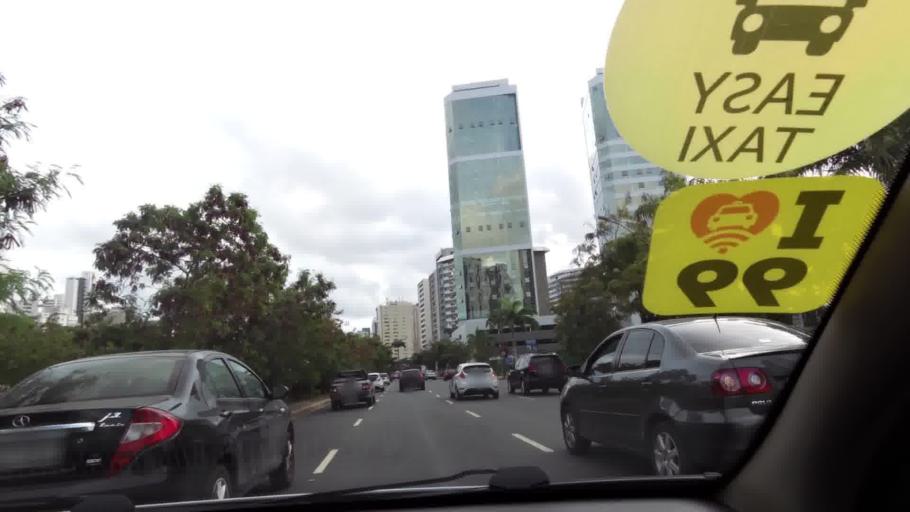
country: BR
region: Pernambuco
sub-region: Recife
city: Recife
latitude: -8.1160
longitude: -34.9008
